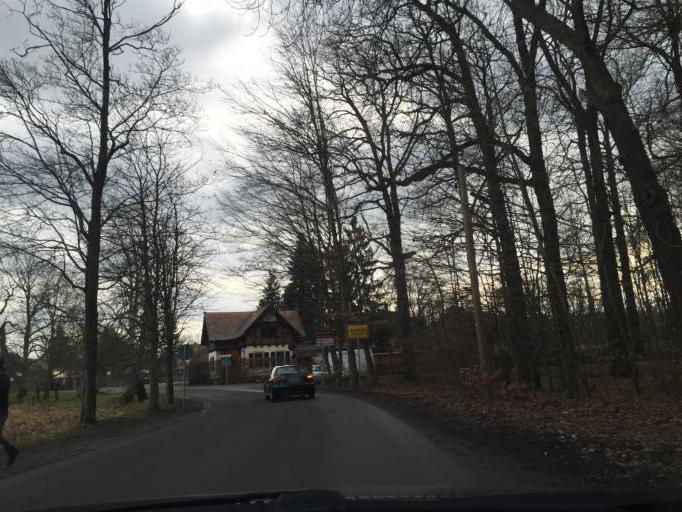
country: DE
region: Saxony
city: Moritzburg
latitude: 51.1669
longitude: 13.6731
